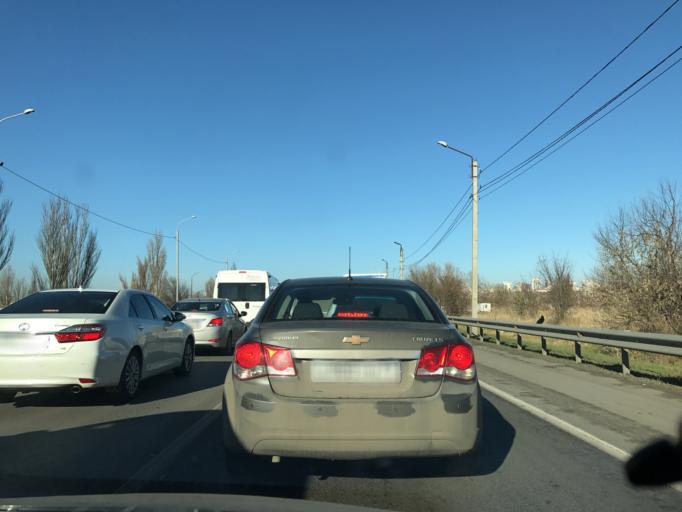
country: RU
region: Rostov
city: Rostov-na-Donu
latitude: 47.1952
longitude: 39.7321
